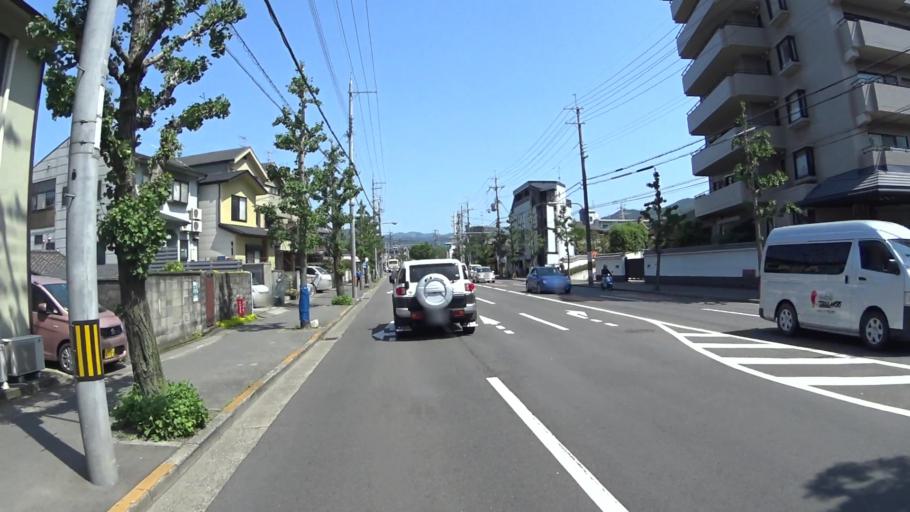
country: JP
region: Kyoto
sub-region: Kyoto-shi
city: Kamigyo-ku
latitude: 35.0587
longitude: 135.7918
